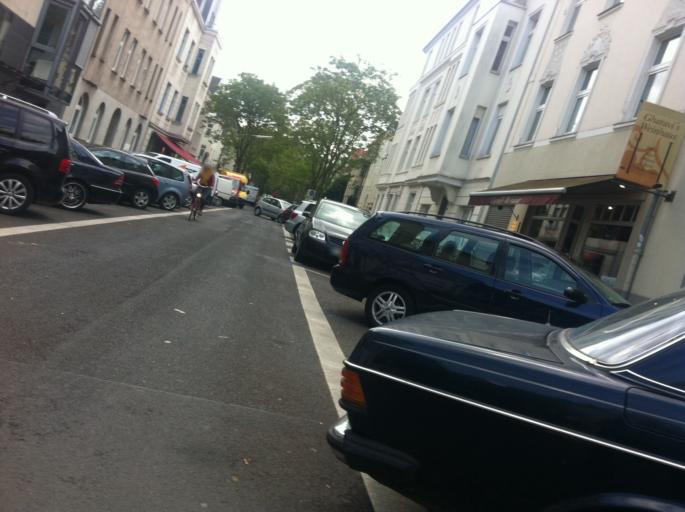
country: DE
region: North Rhine-Westphalia
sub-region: Regierungsbezirk Koln
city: Bilderstoeckchen
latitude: 50.9573
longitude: 6.9197
